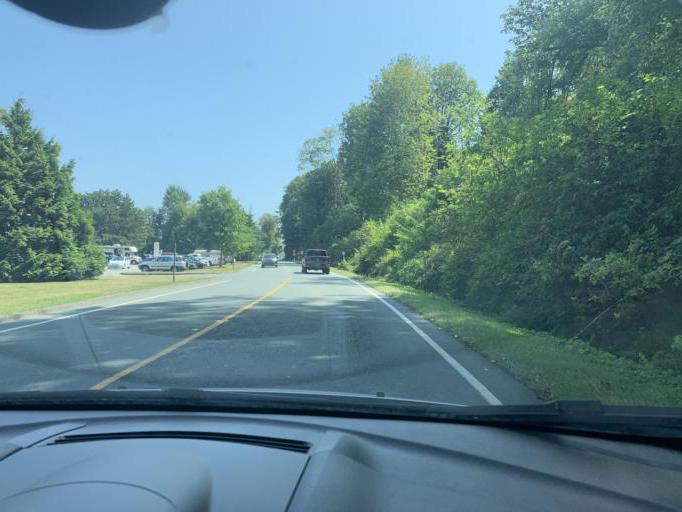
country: CA
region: British Columbia
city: West End
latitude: 49.2776
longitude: -123.2264
